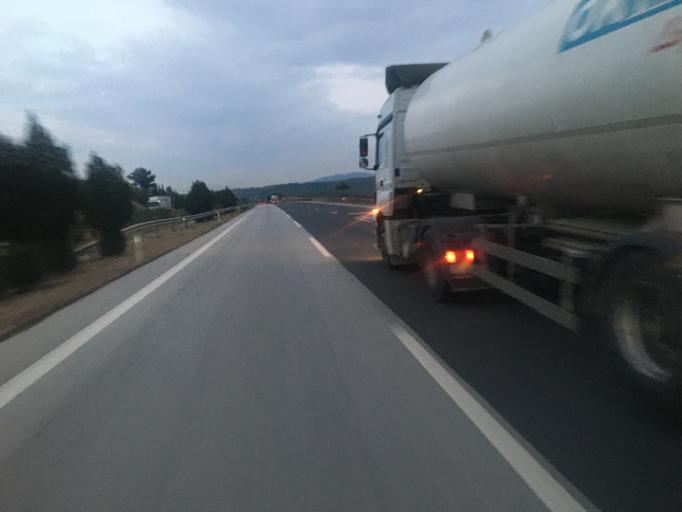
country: TR
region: Osmaniye
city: Kaypak
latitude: 37.1581
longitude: 36.3551
